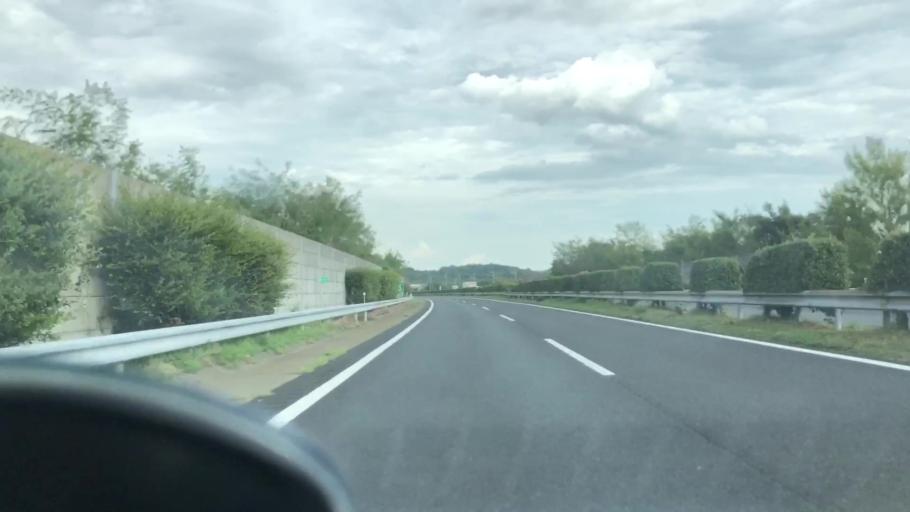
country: JP
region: Hyogo
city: Yashiro
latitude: 34.9289
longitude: 134.9070
